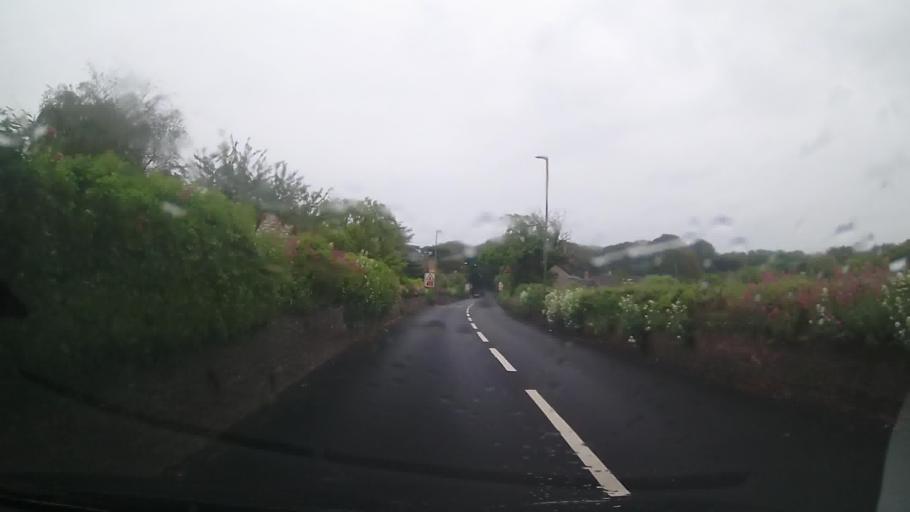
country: GB
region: England
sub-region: Borough of Torbay
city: Brixham
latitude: 50.3923
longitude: -3.5491
